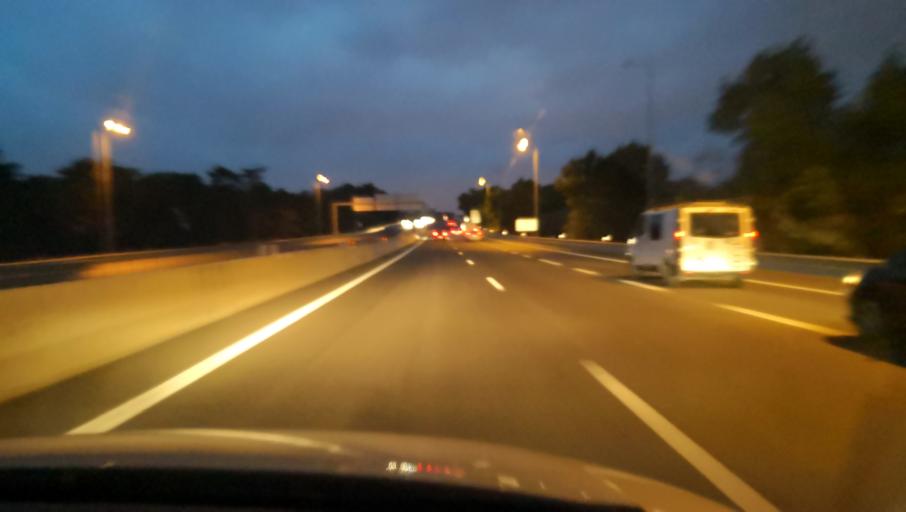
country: PT
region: Setubal
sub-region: Barreiro
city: Santo Antonio da Charneca
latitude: 38.6072
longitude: -9.0224
